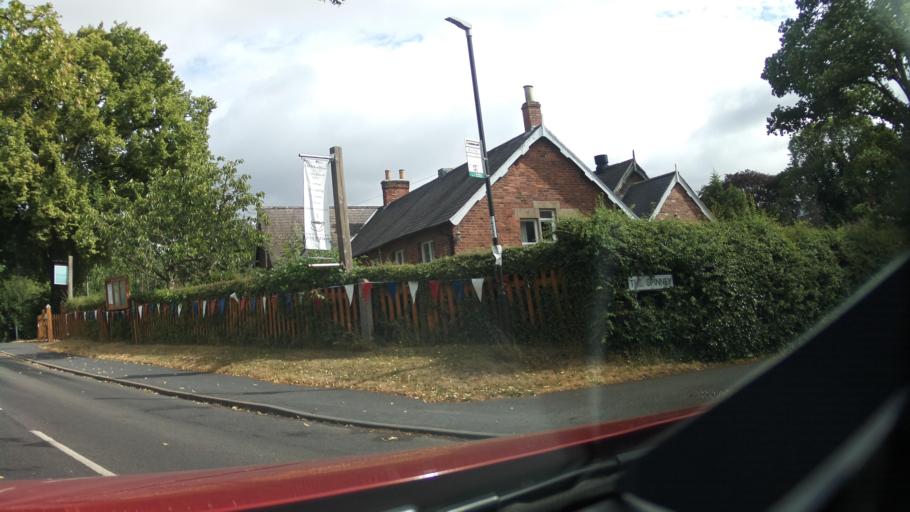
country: GB
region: England
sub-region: Derbyshire
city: Ilkeston
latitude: 52.9361
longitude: -1.3067
